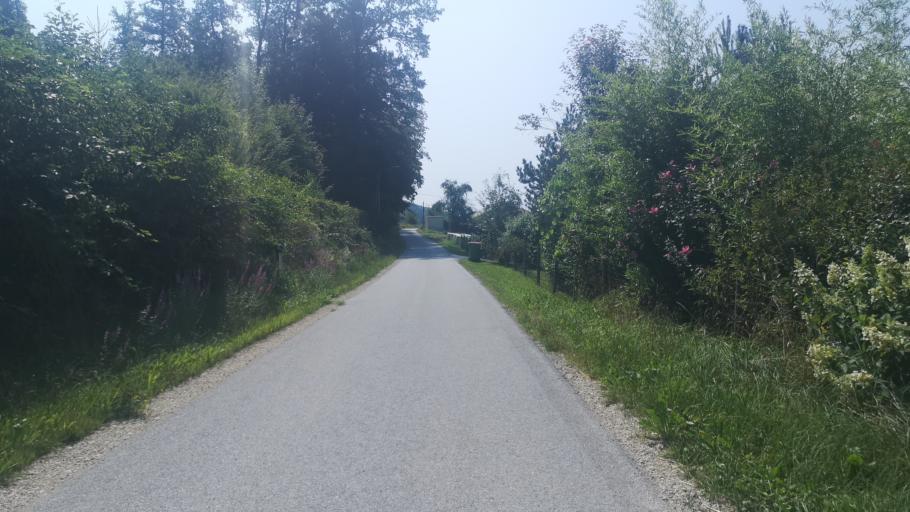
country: AT
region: Styria
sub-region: Politischer Bezirk Deutschlandsberg
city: Lannach
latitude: 46.9349
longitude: 15.3423
